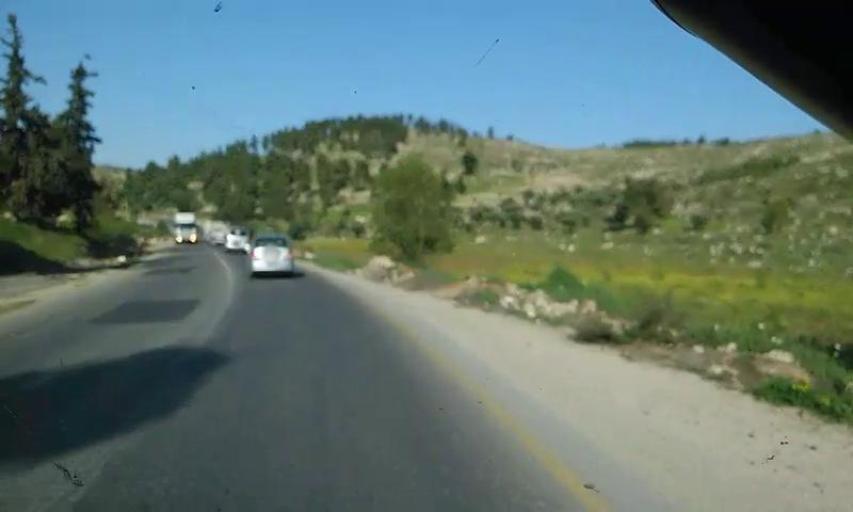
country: PS
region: West Bank
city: Ar Rihiyah
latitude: 31.4883
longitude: 35.0659
